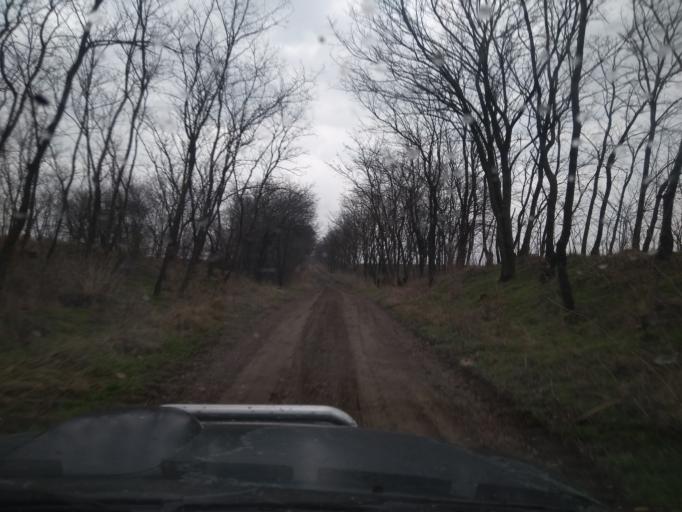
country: HU
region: Szabolcs-Szatmar-Bereg
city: Nagycserkesz
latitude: 47.9804
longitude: 21.5522
